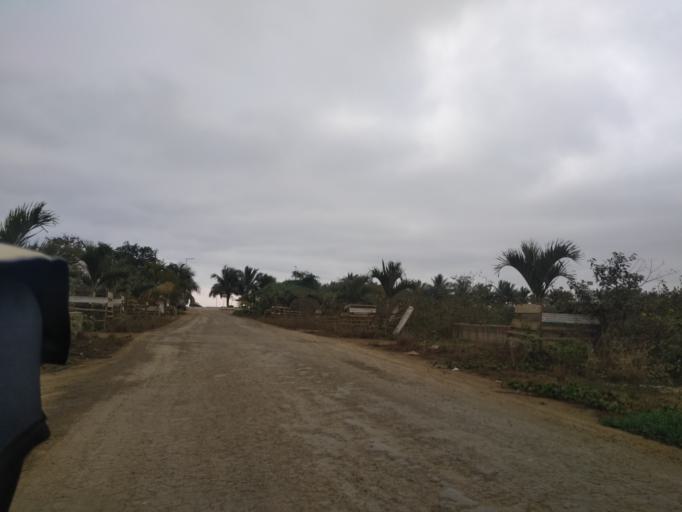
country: EC
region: Manabi
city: Jipijapa
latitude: -1.5511
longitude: -80.8098
